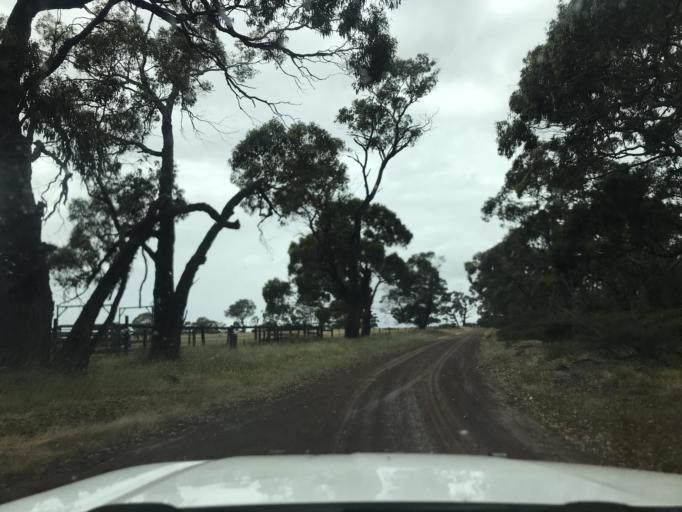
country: AU
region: South Australia
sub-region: Wattle Range
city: Penola
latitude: -37.2313
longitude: 141.3985
